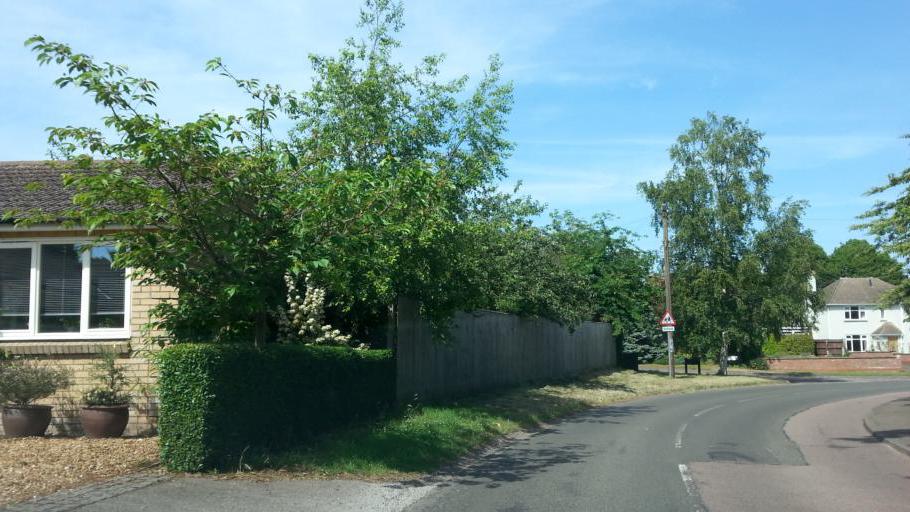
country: GB
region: England
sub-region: Cambridgeshire
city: Sawston
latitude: 52.1459
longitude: 0.1473
